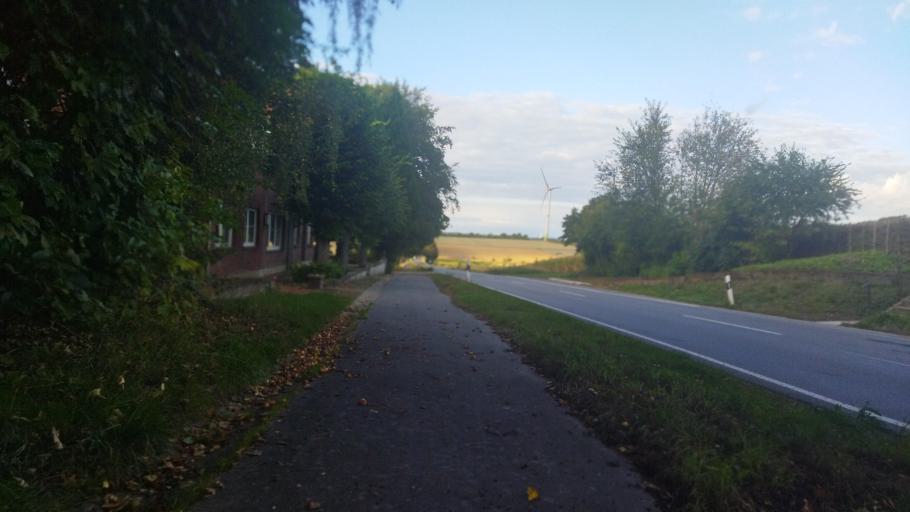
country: DE
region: North Rhine-Westphalia
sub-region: Regierungsbezirk Munster
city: Billerbeck
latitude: 51.9430
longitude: 7.2620
